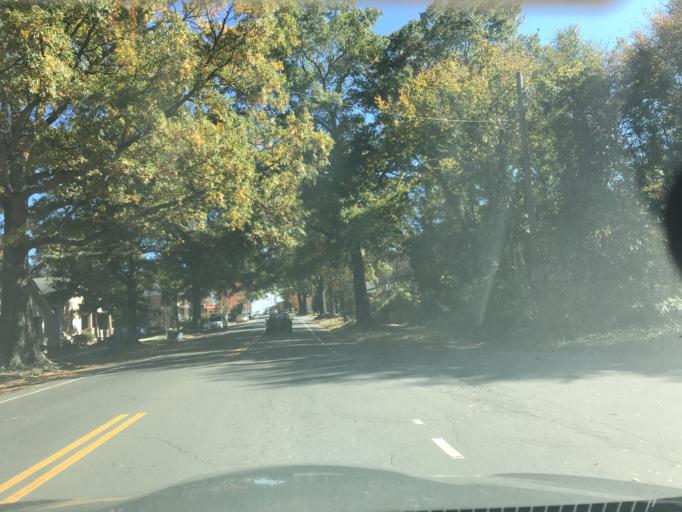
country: US
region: North Carolina
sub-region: Durham County
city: Durham
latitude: 35.9967
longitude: -78.9204
